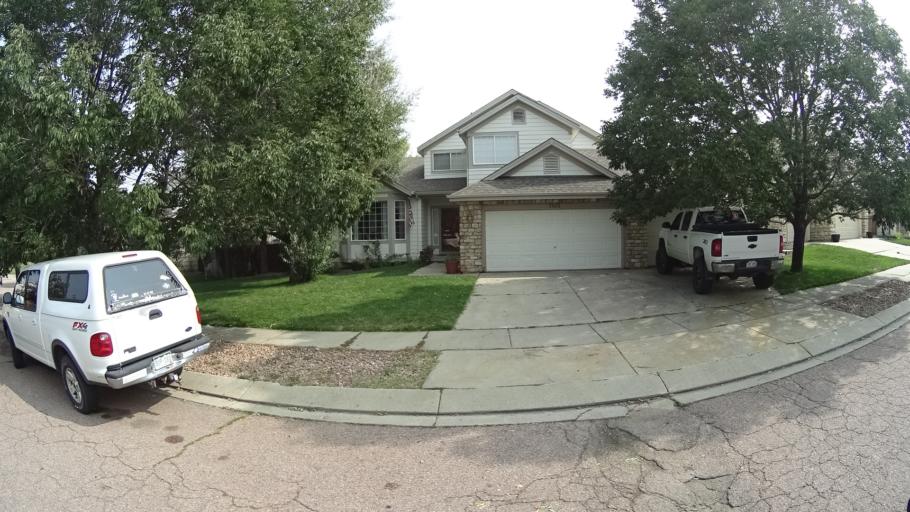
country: US
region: Colorado
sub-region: El Paso County
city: Cimarron Hills
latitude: 38.9175
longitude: -104.7398
